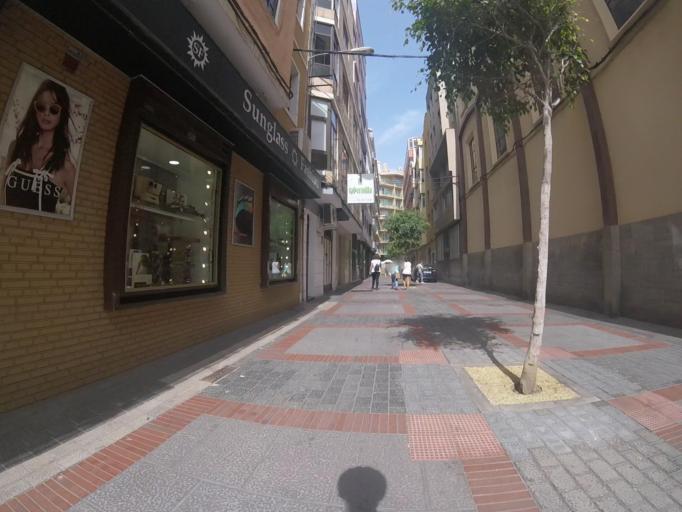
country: ES
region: Canary Islands
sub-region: Provincia de Las Palmas
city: Las Palmas de Gran Canaria
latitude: 28.1413
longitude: -15.4332
